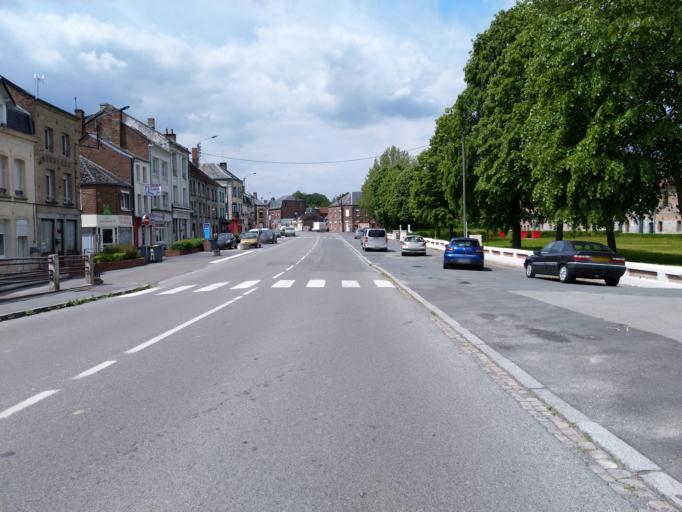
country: FR
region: Nord-Pas-de-Calais
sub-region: Departement du Nord
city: Landrecies
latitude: 50.1271
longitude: 3.6875
